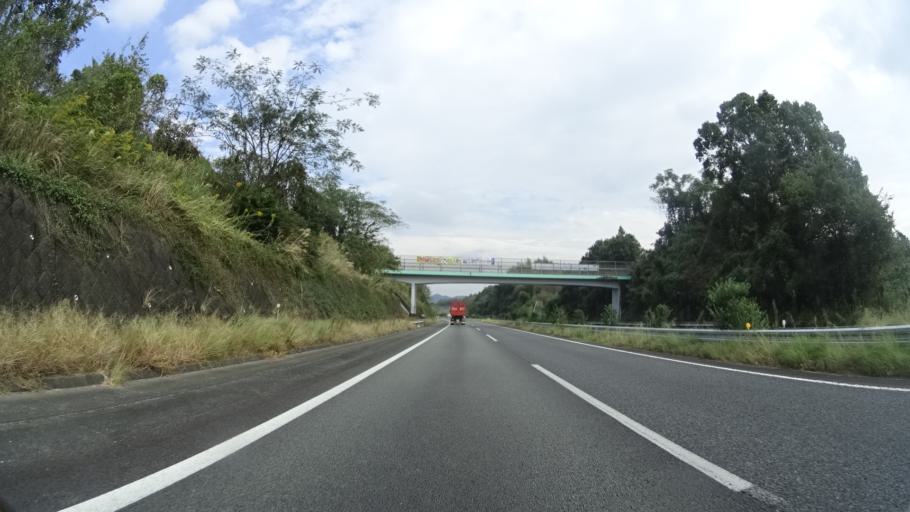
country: JP
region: Kumamoto
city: Matsubase
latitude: 32.5628
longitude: 130.6999
